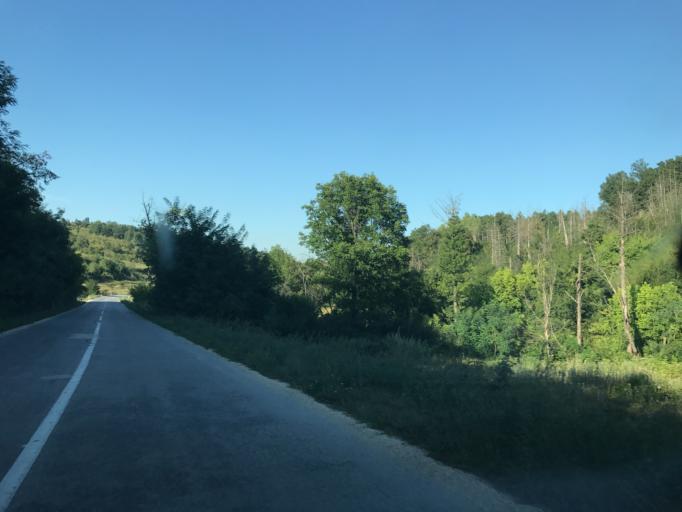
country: RO
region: Mehedinti
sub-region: Comuna Gogosu
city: Ostrovu Mare
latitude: 44.2864
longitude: 22.3231
